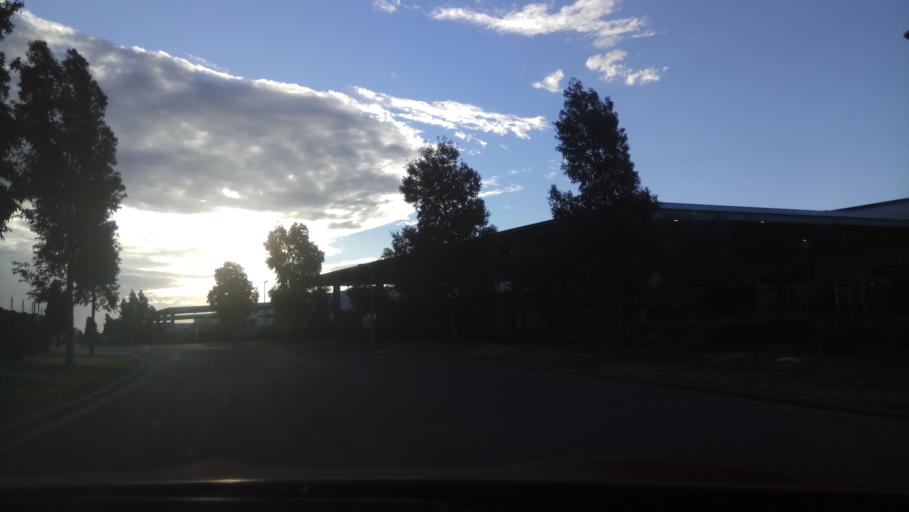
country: AU
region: Victoria
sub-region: Hobsons Bay
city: Altona
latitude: -37.8514
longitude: 144.8293
